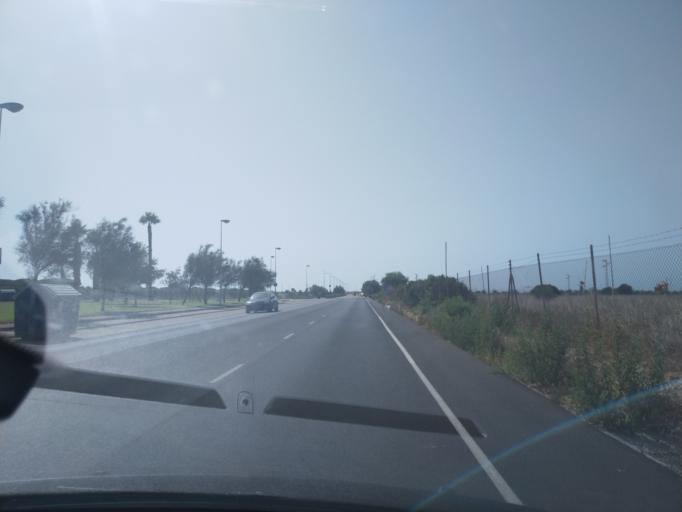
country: ES
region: Andalusia
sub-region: Provincia de Cadiz
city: Chiclana de la Frontera
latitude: 36.3854
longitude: -6.2024
